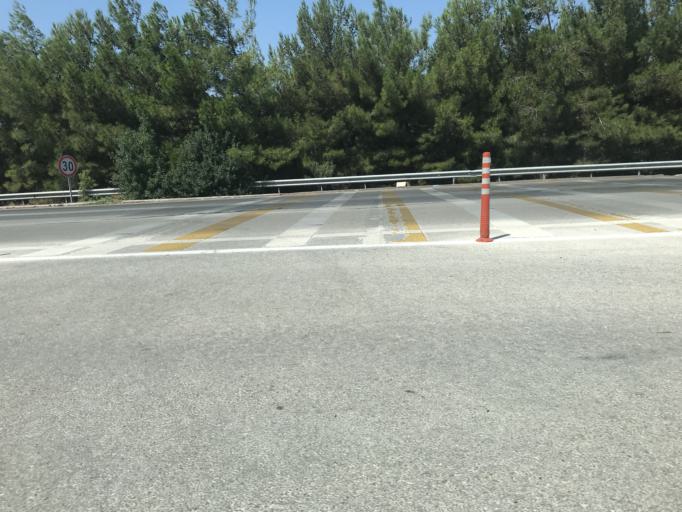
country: TR
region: Izmir
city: Urla
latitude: 38.3232
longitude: 26.7820
